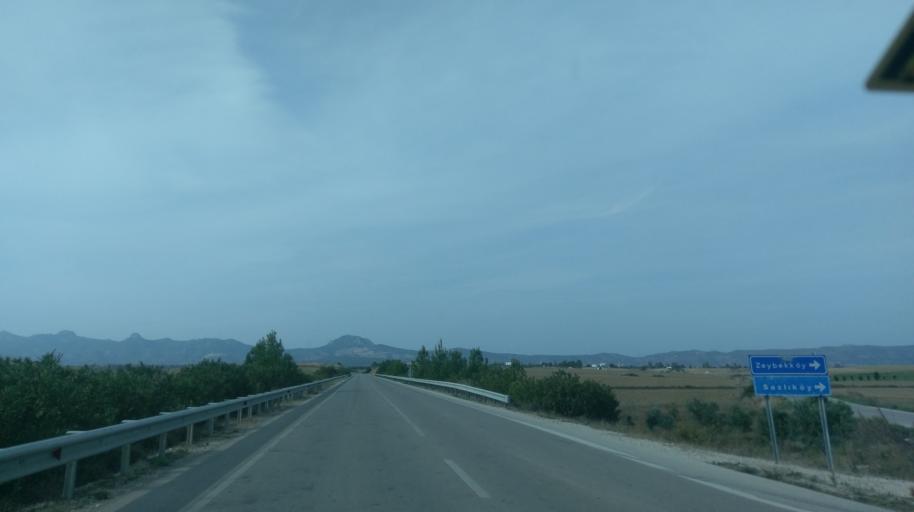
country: CY
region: Ammochostos
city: Leonarisso
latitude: 35.3801
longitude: 34.0217
